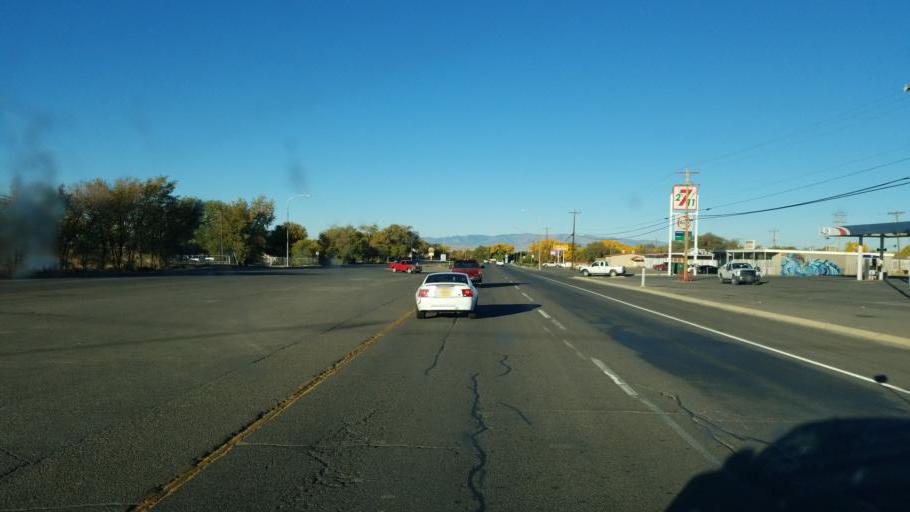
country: US
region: New Mexico
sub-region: San Juan County
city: Shiprock
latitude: 36.7843
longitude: -108.6683
